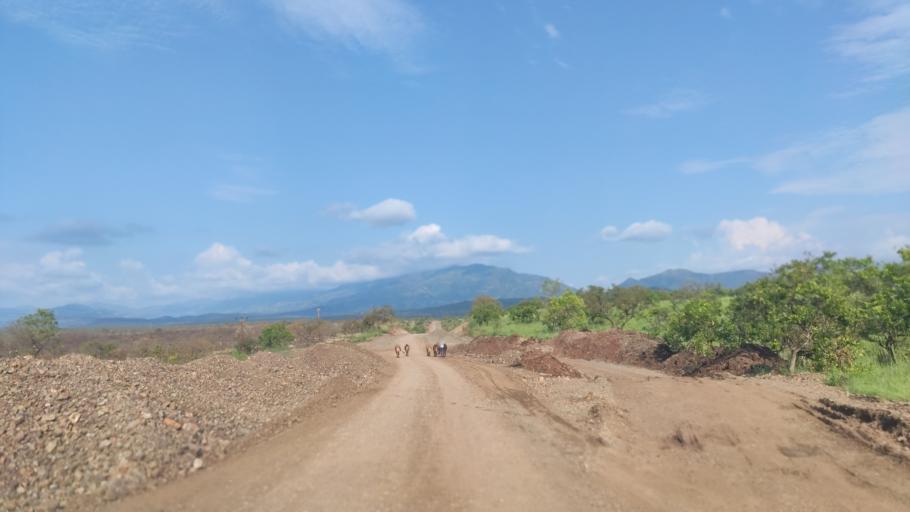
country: ET
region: Southern Nations, Nationalities, and People's Region
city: Felege Neway
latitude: 6.4251
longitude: 37.2481
